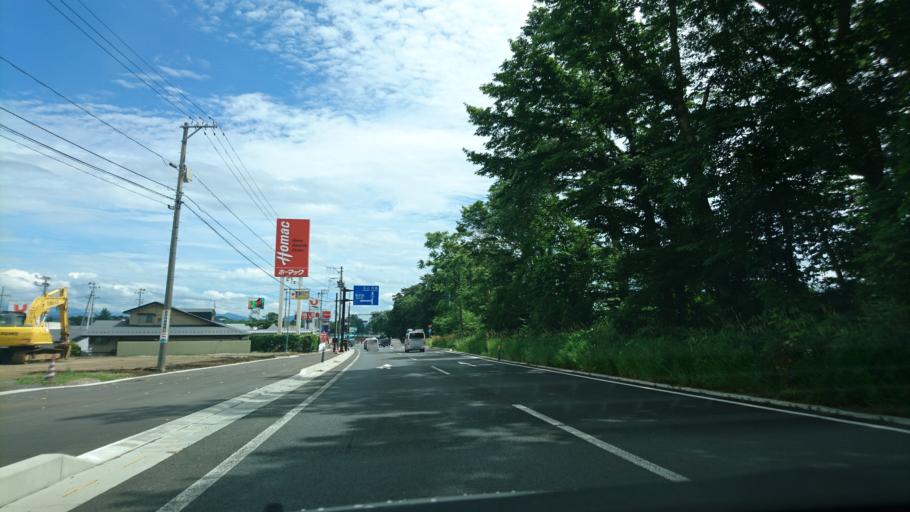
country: JP
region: Iwate
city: Morioka-shi
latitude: 39.7752
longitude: 141.1273
